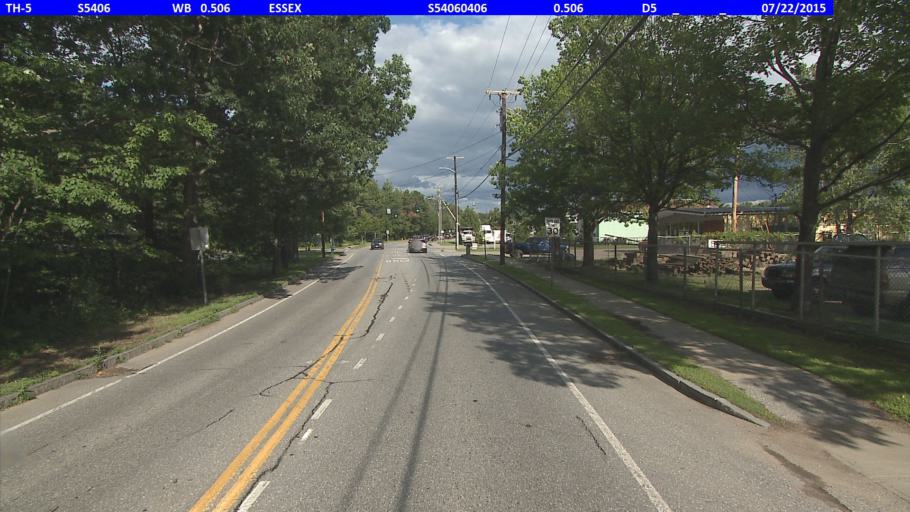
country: US
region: Vermont
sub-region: Chittenden County
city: Colchester
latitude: 44.5122
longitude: -73.1404
